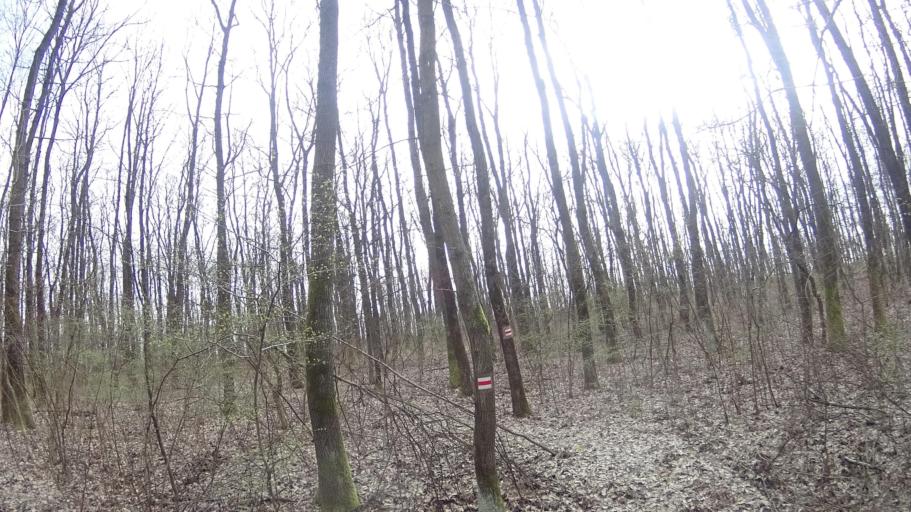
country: HU
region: Pest
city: Veroce
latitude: 47.8278
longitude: 19.0830
